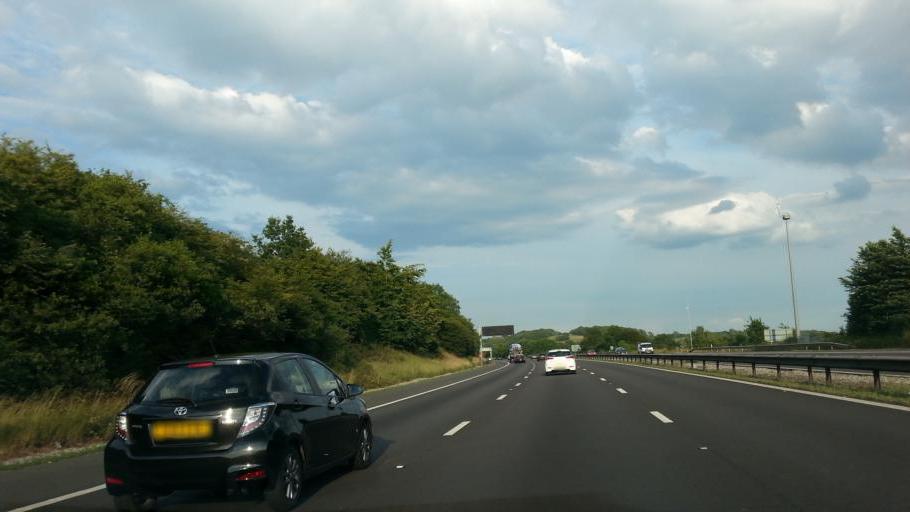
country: GB
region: England
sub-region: Worcestershire
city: Alvechurch
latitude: 52.3557
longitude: -1.9237
